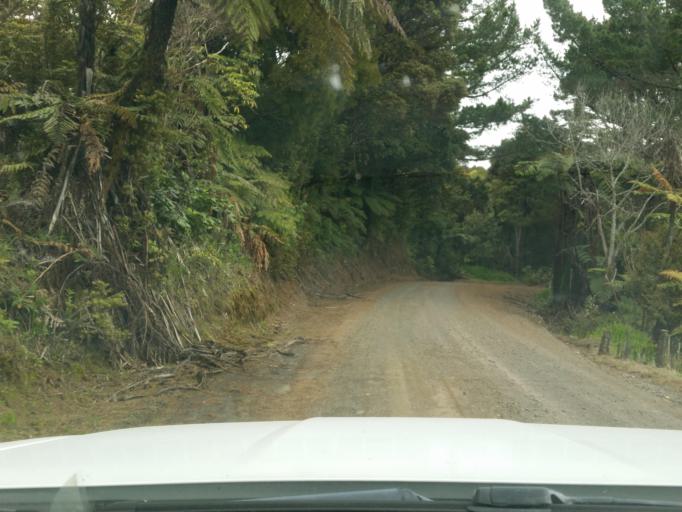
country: NZ
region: Northland
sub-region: Kaipara District
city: Dargaville
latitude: -35.7038
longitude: 173.6412
